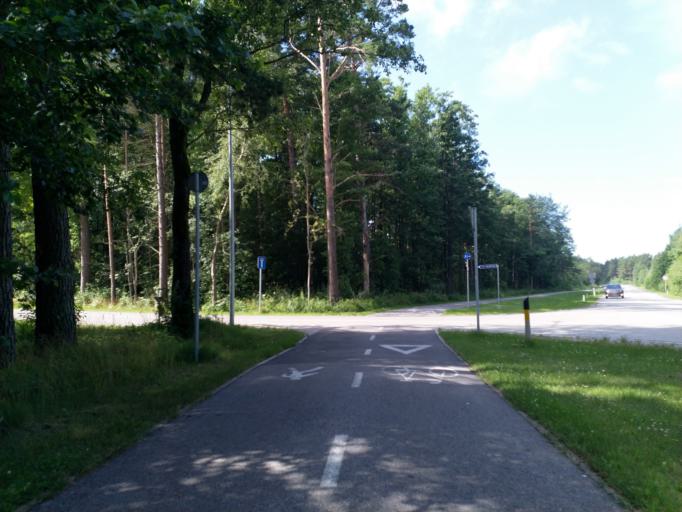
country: LV
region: Ventspils
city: Ventspils
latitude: 57.4200
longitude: 21.6342
